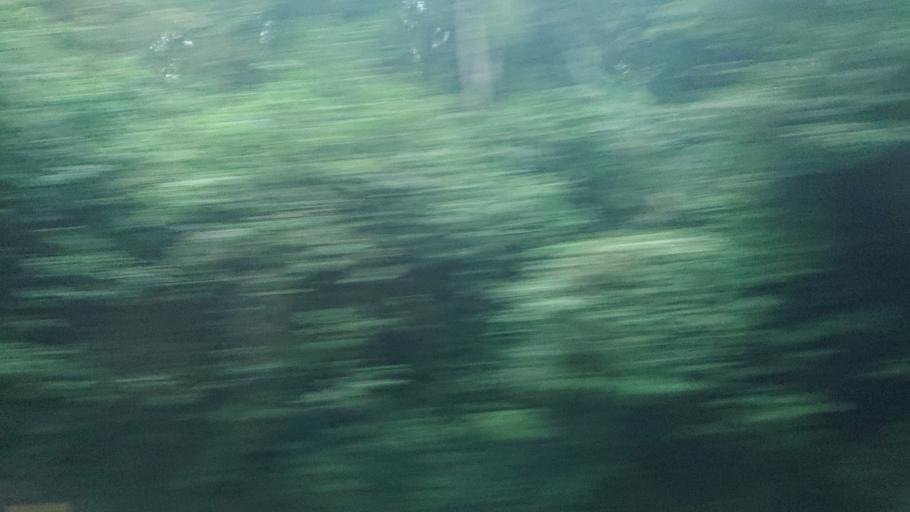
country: TW
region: Taiwan
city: Lugu
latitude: 23.5072
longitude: 120.6964
